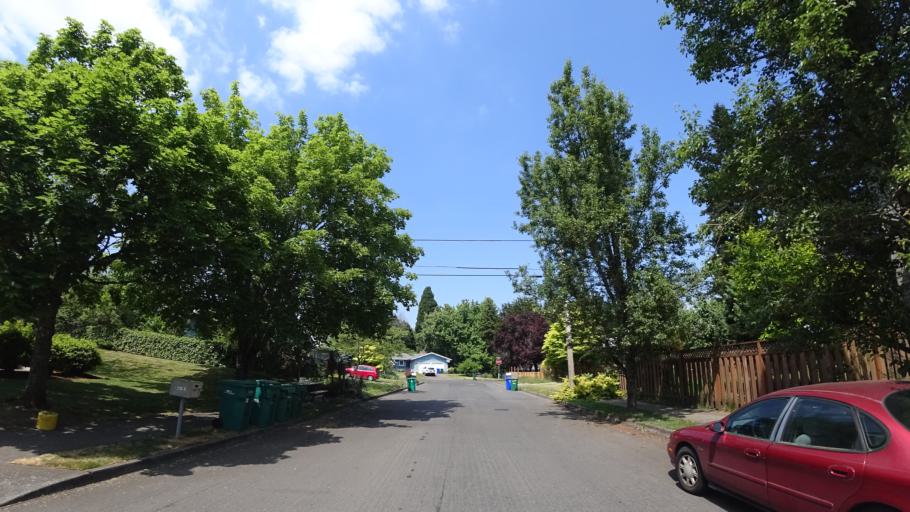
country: US
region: Oregon
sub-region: Multnomah County
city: Fairview
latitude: 45.5299
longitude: -122.4933
